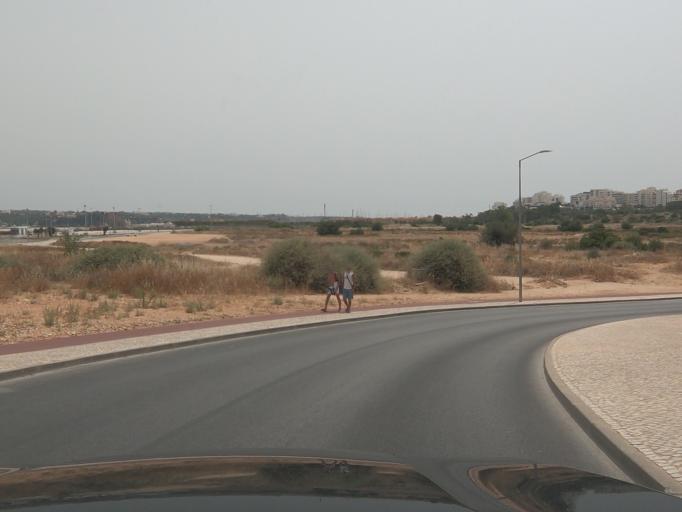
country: PT
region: Faro
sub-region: Portimao
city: Portimao
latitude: 37.1282
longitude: -8.5335
